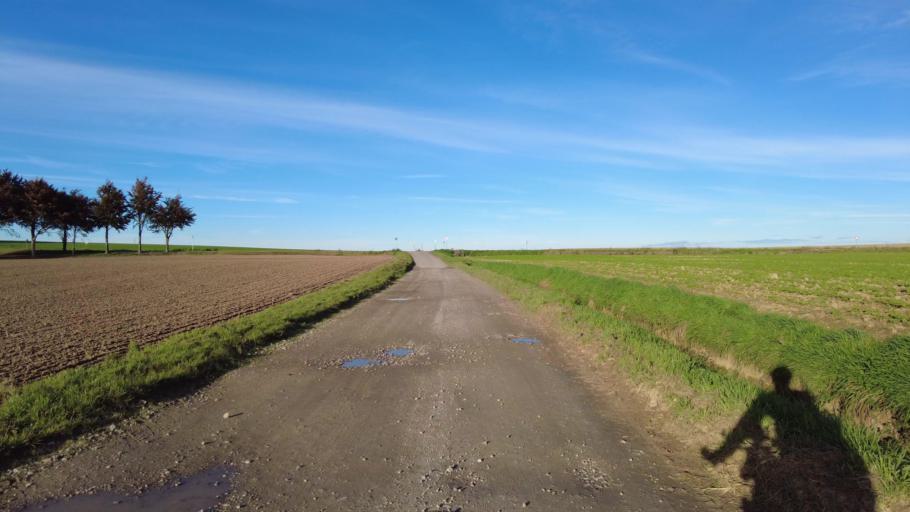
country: BE
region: Wallonia
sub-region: Province du Brabant Wallon
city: Jodoigne
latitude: 50.7103
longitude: 4.9013
